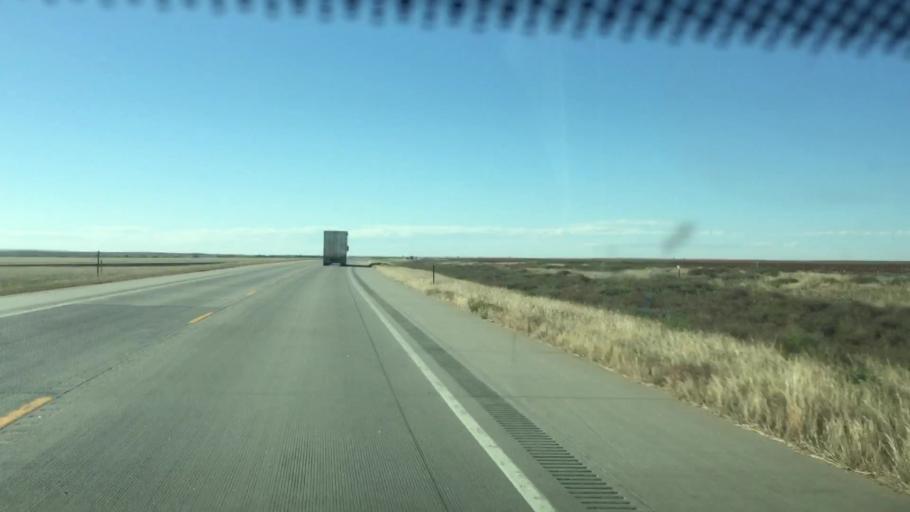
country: US
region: Colorado
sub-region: Kiowa County
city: Eads
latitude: 38.7890
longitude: -102.9301
